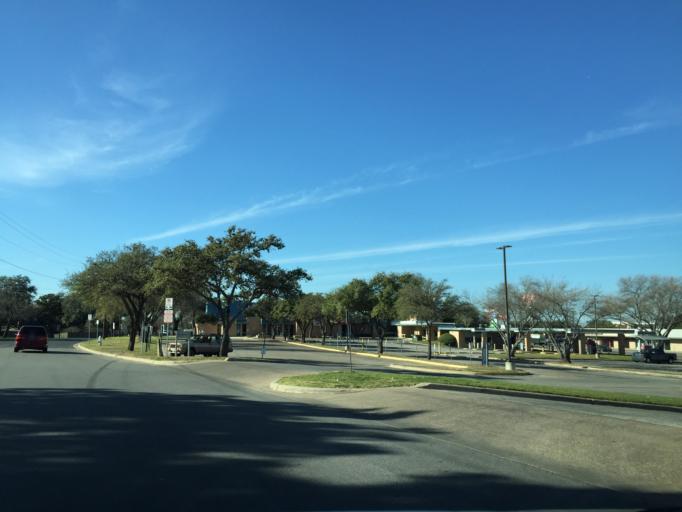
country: US
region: Texas
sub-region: Travis County
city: Austin
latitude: 30.2364
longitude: -97.7533
